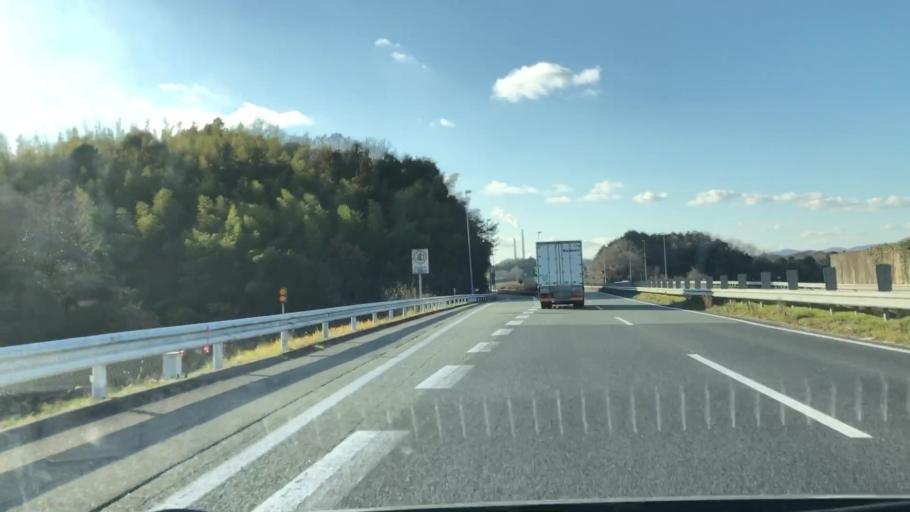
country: JP
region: Yamaguchi
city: Ogori-shimogo
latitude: 34.1704
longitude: 131.2500
